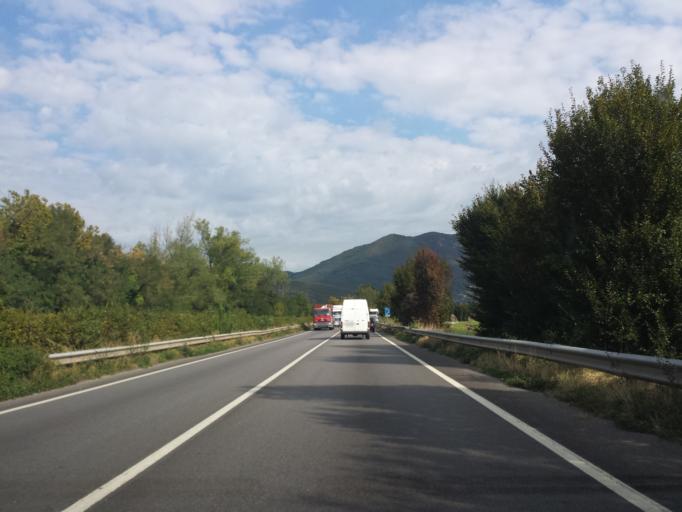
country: IT
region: Lombardy
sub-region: Provincia di Brescia
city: Gavardo-Sopraponte
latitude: 45.5698
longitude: 10.4420
